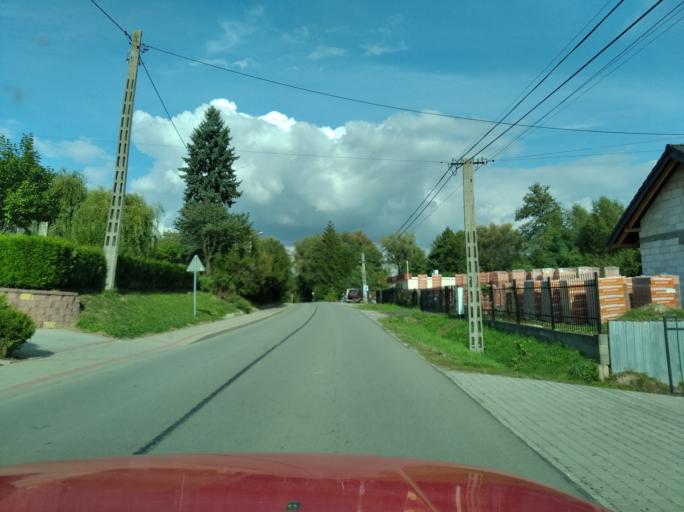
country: PL
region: Subcarpathian Voivodeship
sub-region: Powiat rzeszowski
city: Tyczyn
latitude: 49.9424
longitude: 22.0204
